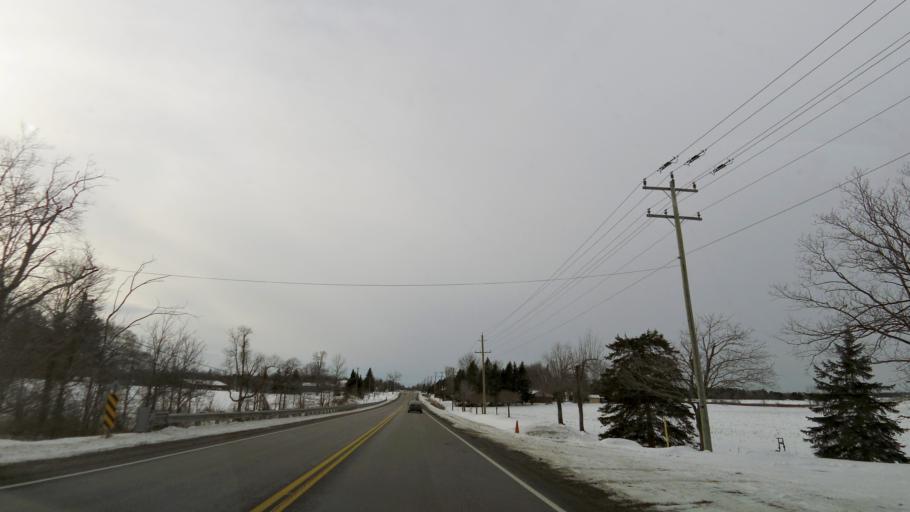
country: CA
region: Ontario
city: Ancaster
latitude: 43.2896
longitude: -80.0179
